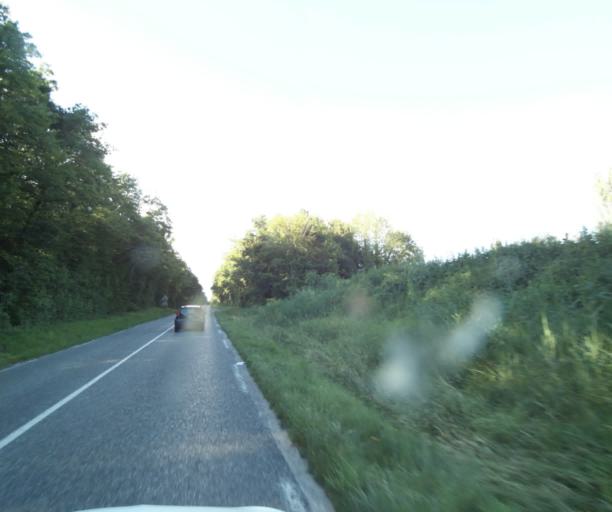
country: FR
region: Rhone-Alpes
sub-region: Departement de la Haute-Savoie
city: Douvaine
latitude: 46.3265
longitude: 6.2924
